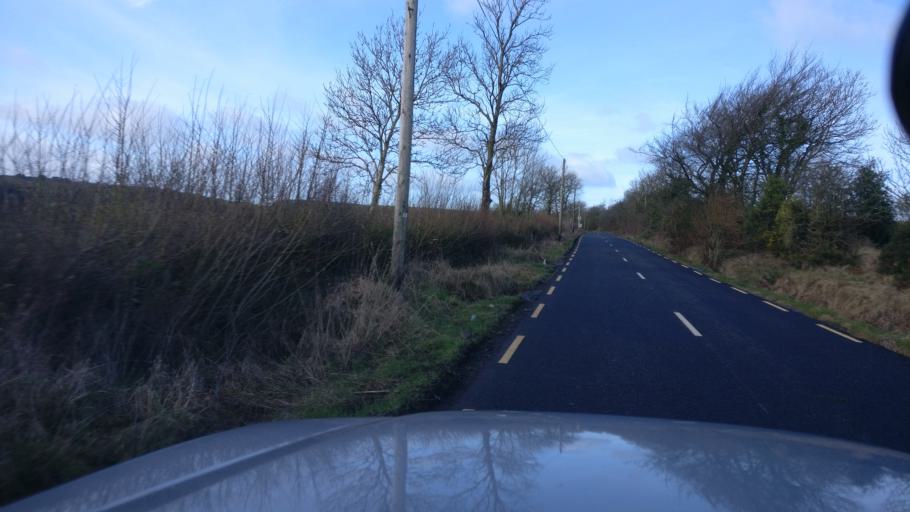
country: IE
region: Leinster
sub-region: Kilkenny
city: Castlecomer
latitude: 52.8998
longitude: -7.1753
